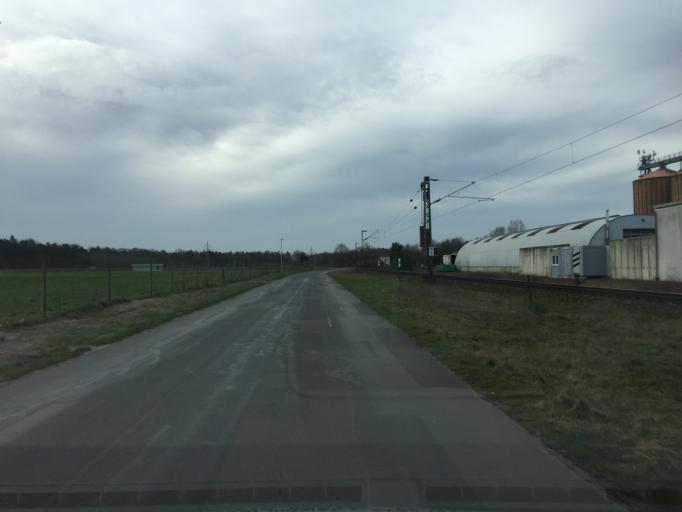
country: DE
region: Lower Saxony
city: Leese
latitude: 52.5243
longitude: 9.1255
